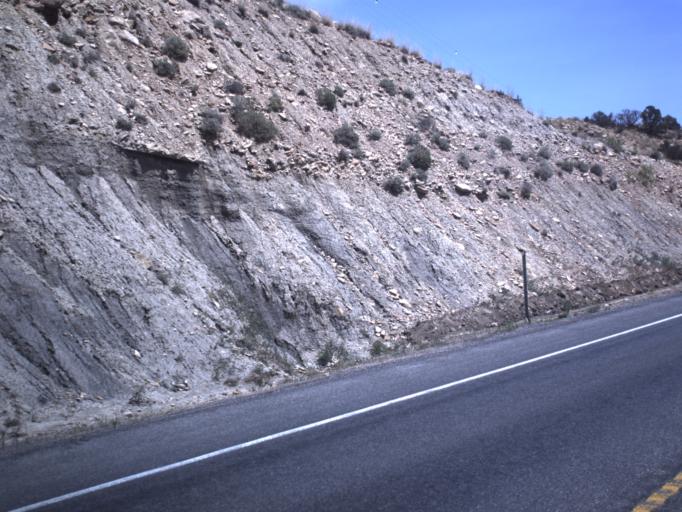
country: US
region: Utah
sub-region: Emery County
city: Huntington
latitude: 39.3749
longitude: -111.0652
